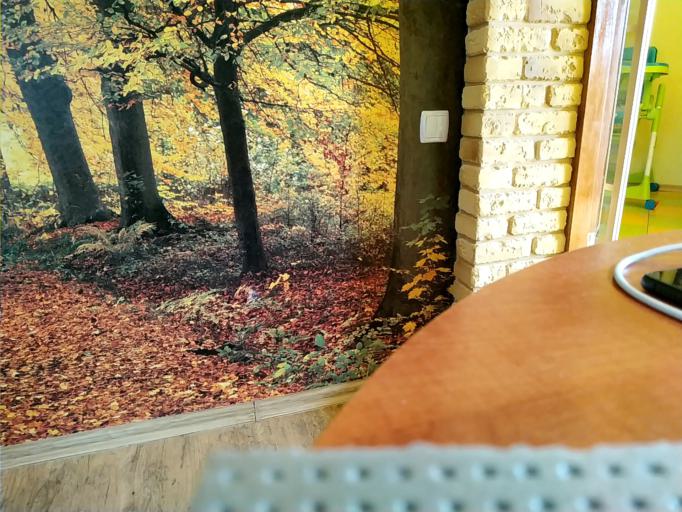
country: RU
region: Tverskaya
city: Kalashnikovo
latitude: 57.3519
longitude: 35.1694
